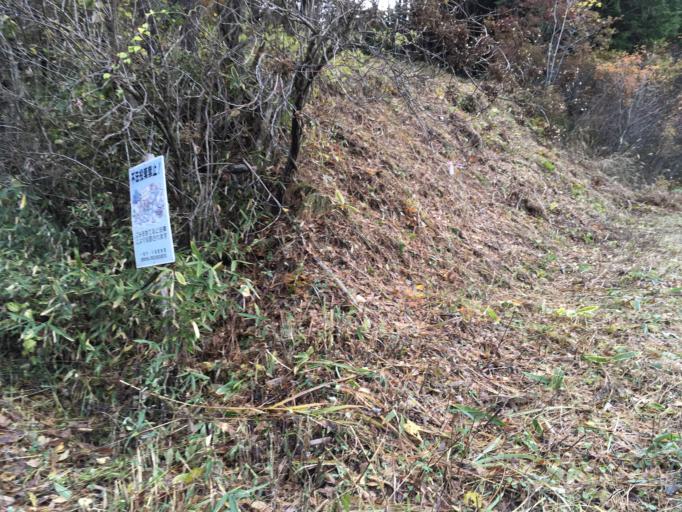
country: JP
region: Iwate
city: Ofunato
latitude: 38.8876
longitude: 141.4669
